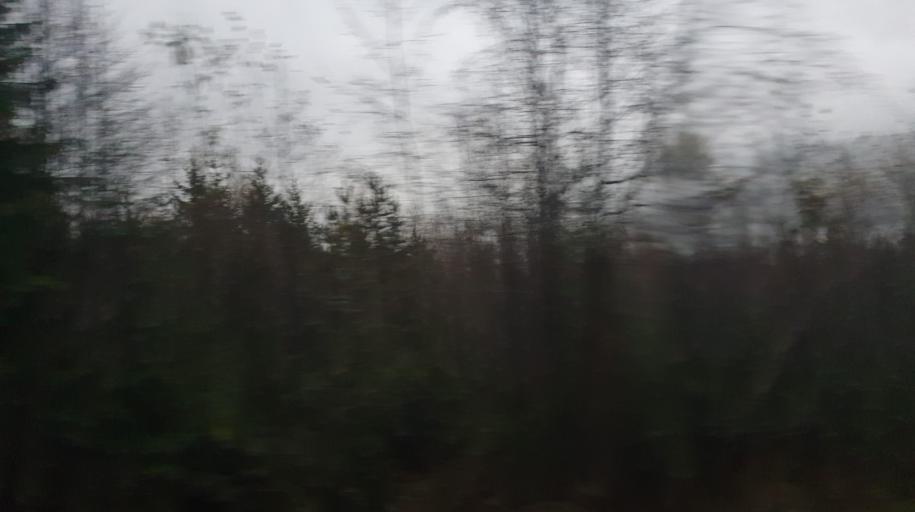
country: NO
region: Buskerud
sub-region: Krodsherad
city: Noresund
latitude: 60.1891
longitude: 9.5940
